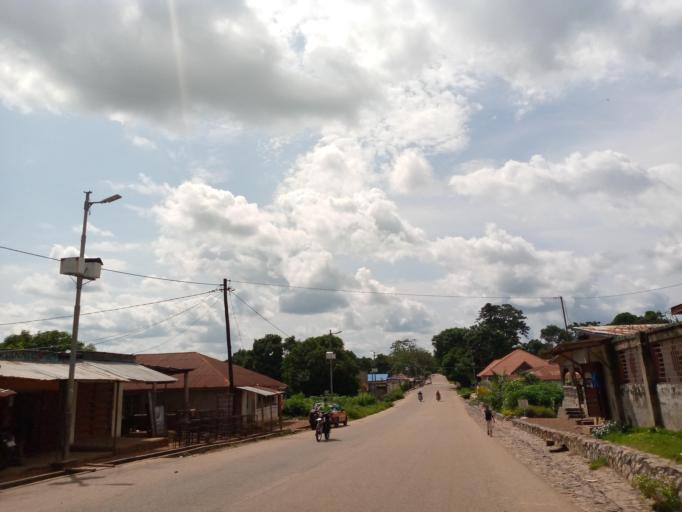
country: SL
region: Northern Province
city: Magburaka
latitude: 8.7162
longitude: -11.9372
